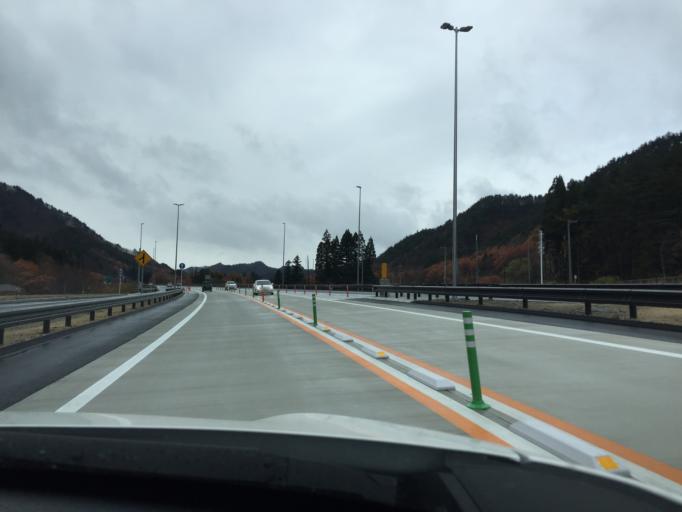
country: JP
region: Yamagata
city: Yonezawa
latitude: 37.8699
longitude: 140.2229
